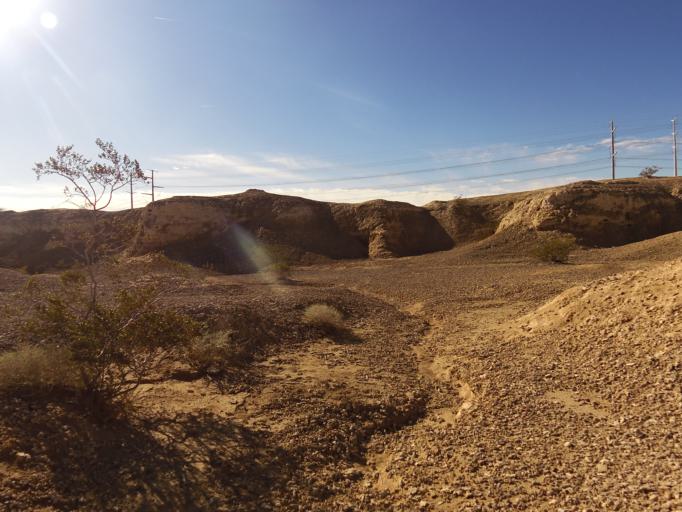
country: US
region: Nevada
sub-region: Clark County
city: North Las Vegas
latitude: 36.3377
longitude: -115.2769
